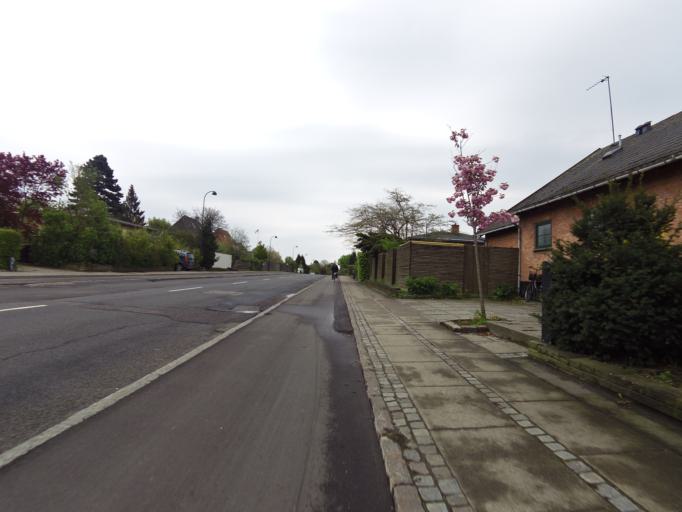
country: DK
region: Capital Region
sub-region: Gentofte Kommune
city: Charlottenlund
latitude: 55.7325
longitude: 12.5483
